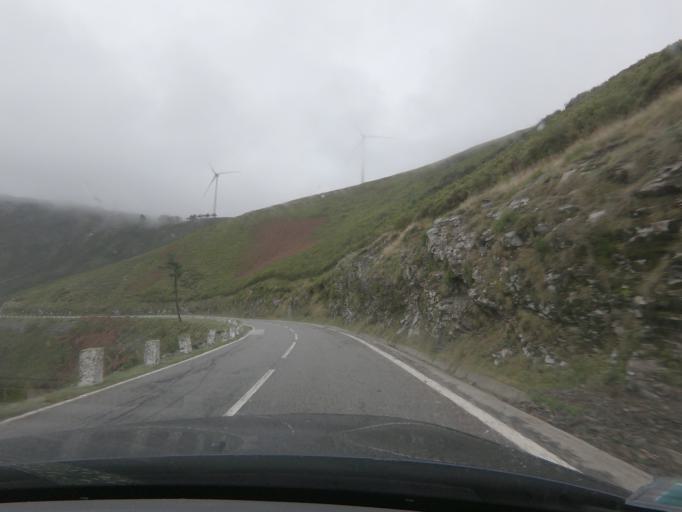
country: PT
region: Vila Real
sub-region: Mondim de Basto
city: Mondim de Basto
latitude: 41.3248
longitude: -7.8828
